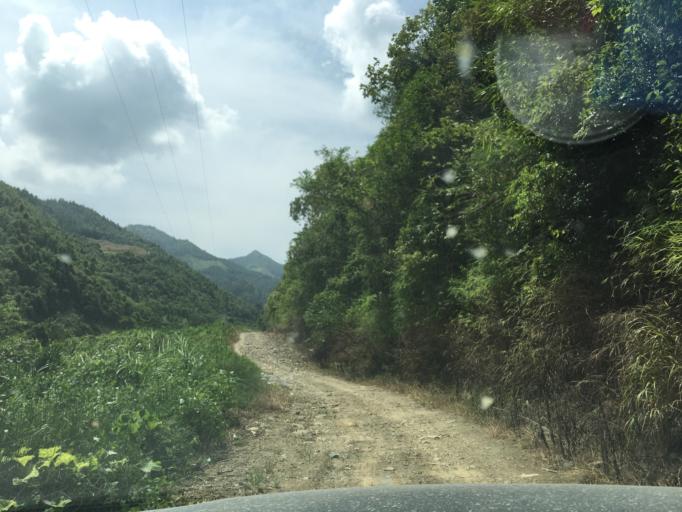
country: CN
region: Guangxi Zhuangzu Zizhiqu
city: Xinzhou
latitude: 24.9536
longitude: 105.7961
